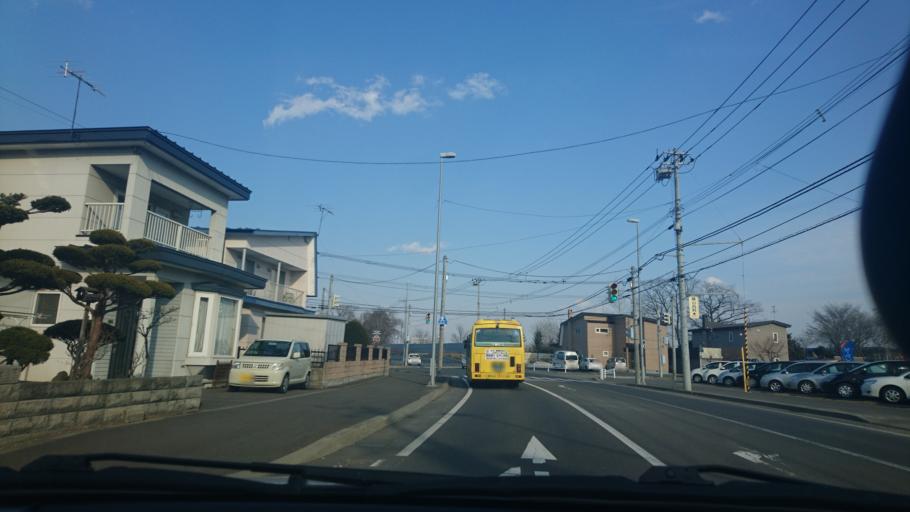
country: JP
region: Hokkaido
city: Obihiro
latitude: 42.9239
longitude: 143.1771
